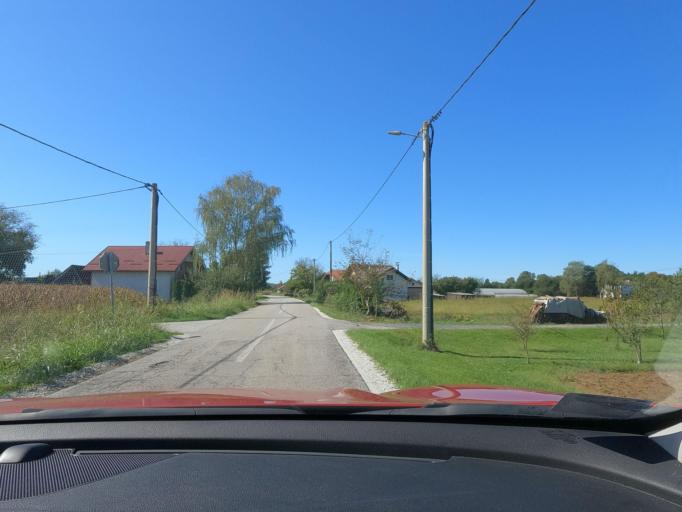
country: HR
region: Sisacko-Moslavacka
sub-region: Grad Sisak
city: Sisak
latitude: 45.4886
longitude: 16.3368
